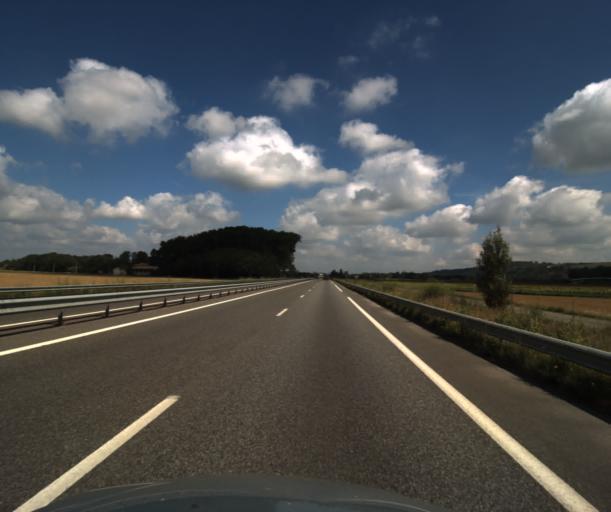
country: FR
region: Midi-Pyrenees
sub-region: Departement de la Haute-Garonne
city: Labarthe-sur-Leze
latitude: 43.4639
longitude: 1.4129
